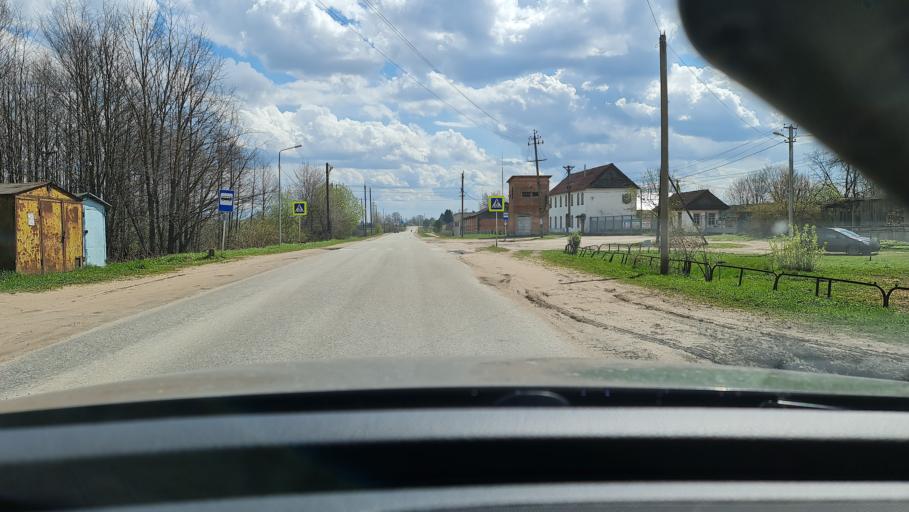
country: RU
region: Tverskaya
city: Toropets
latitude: 56.4878
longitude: 31.6199
